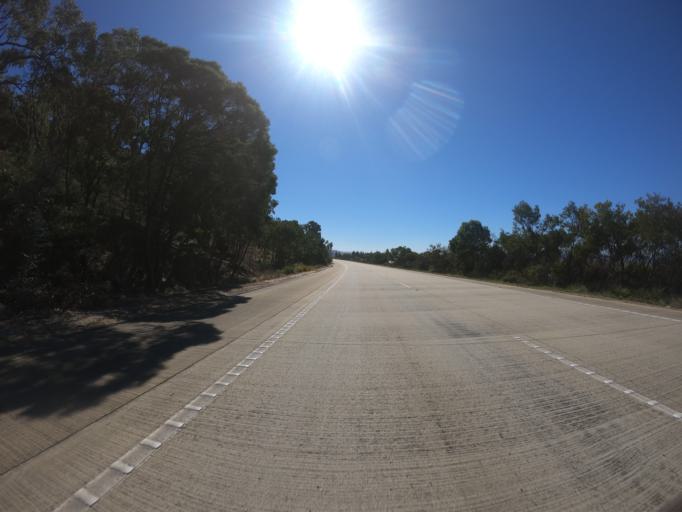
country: AU
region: New South Wales
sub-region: Yass Valley
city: Gundaroo
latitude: -35.0962
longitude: 149.3760
